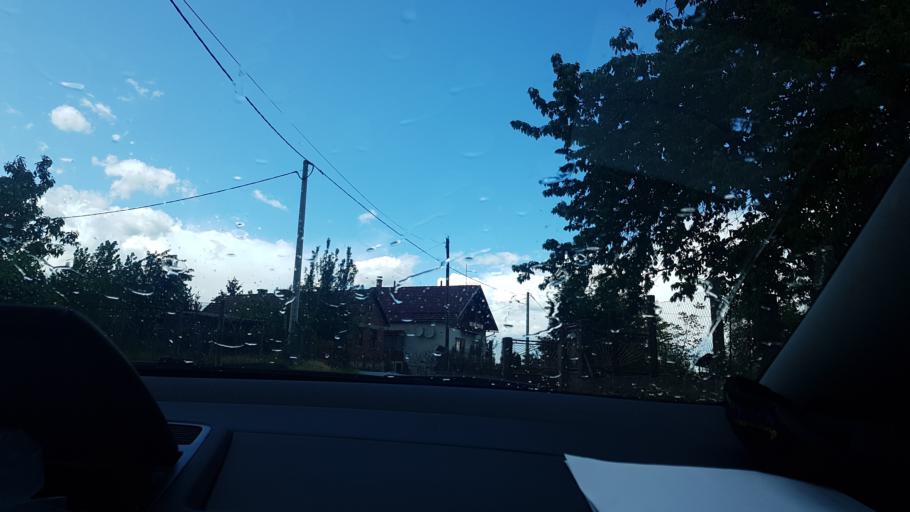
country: HR
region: Varazdinska
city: Ivanec
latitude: 46.2367
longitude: 16.1010
